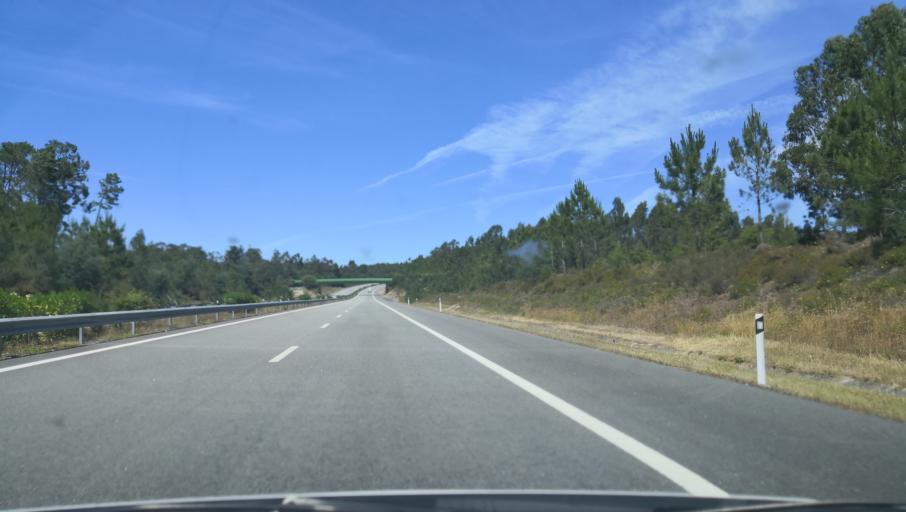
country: PT
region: Coimbra
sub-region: Montemor-O-Velho
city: Arazede
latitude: 40.2404
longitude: -8.6600
